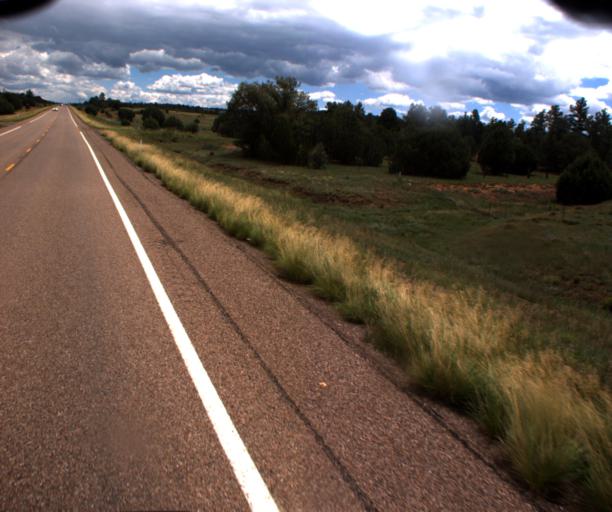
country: US
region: Arizona
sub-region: Navajo County
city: Linden
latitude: 34.3481
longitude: -110.3046
